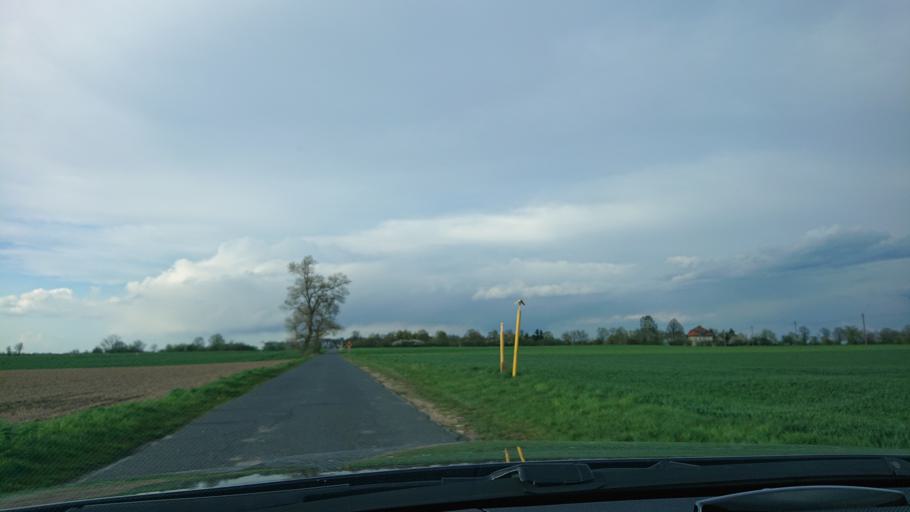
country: PL
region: Greater Poland Voivodeship
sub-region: Powiat gnieznienski
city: Klecko
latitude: 52.5836
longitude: 17.4832
